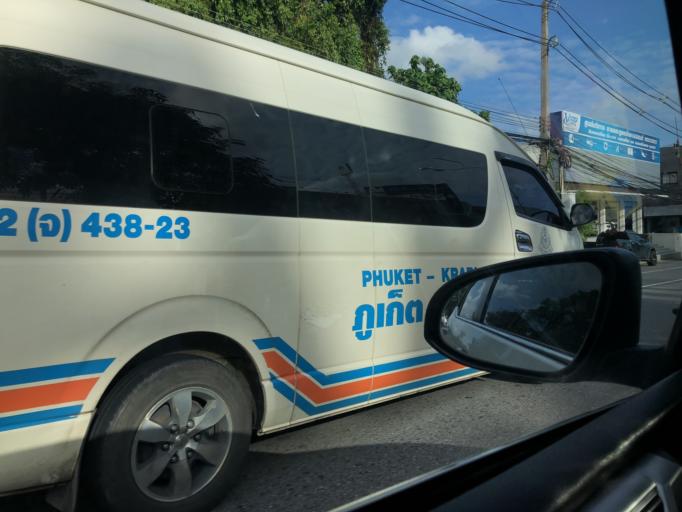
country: TH
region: Phuket
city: Ban Ko Kaeo
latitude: 7.9254
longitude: 98.3959
